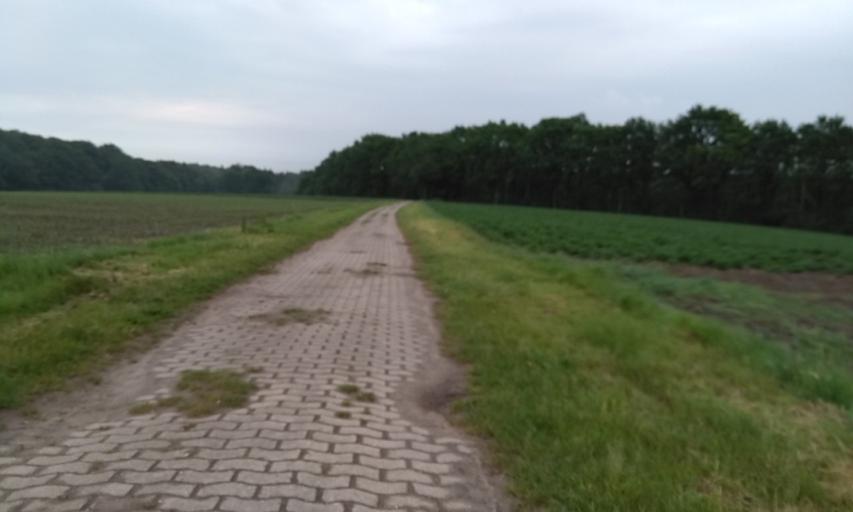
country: DE
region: Lower Saxony
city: Buxtehude
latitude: 53.4653
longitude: 9.6528
